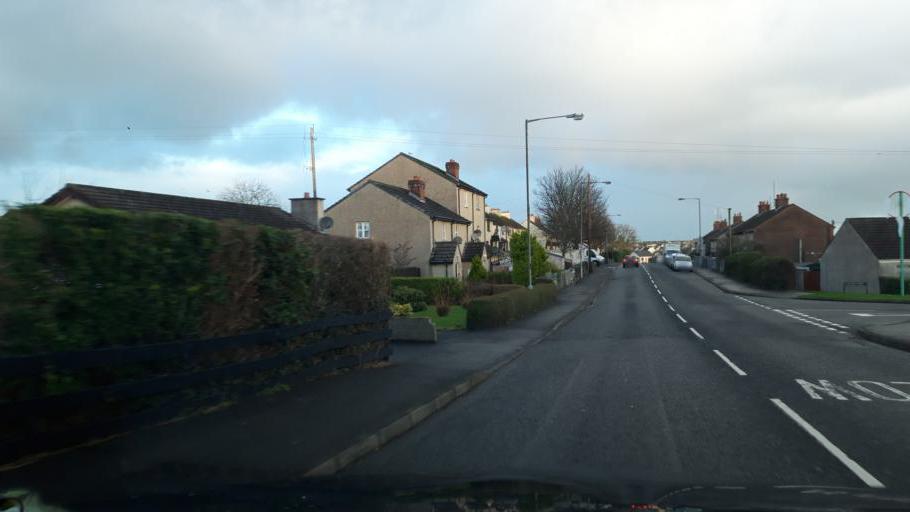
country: GB
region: Northern Ireland
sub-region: Moyle District
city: Ballycastle
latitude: 55.1977
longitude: -6.2617
